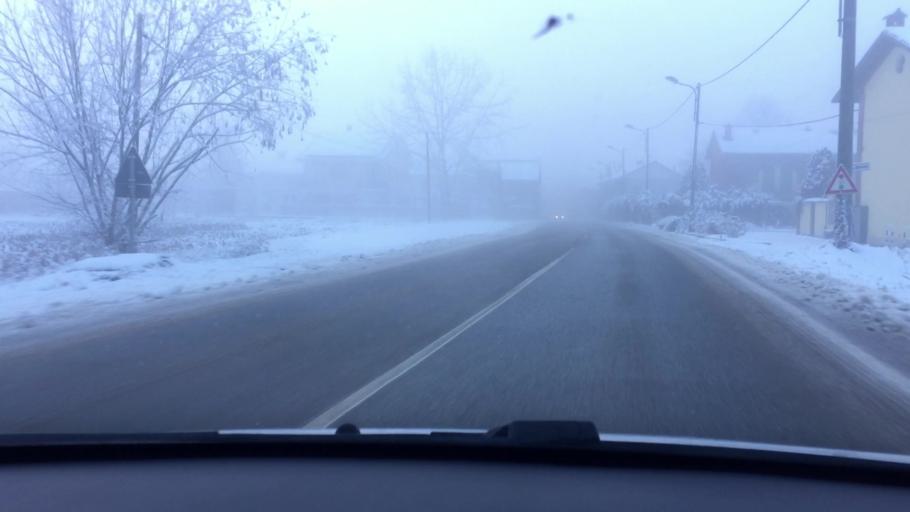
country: IT
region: Piedmont
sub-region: Provincia di Torino
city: Scalenghe
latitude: 44.8974
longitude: 7.4904
